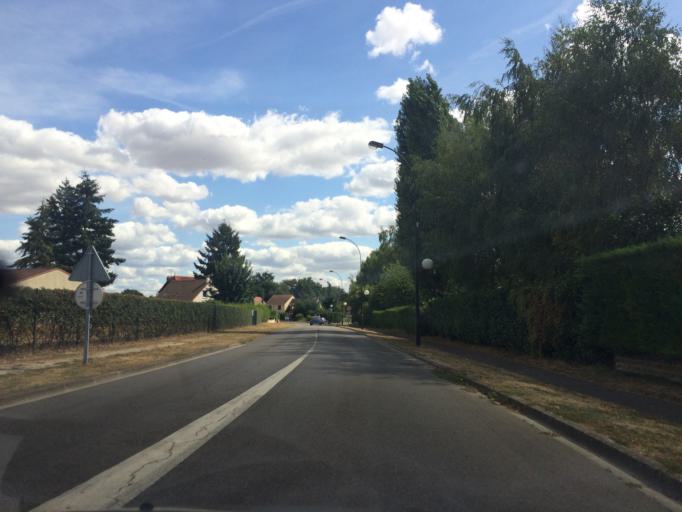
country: FR
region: Ile-de-France
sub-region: Departement de l'Essonne
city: Saint-Vrain
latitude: 48.5444
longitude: 2.3225
